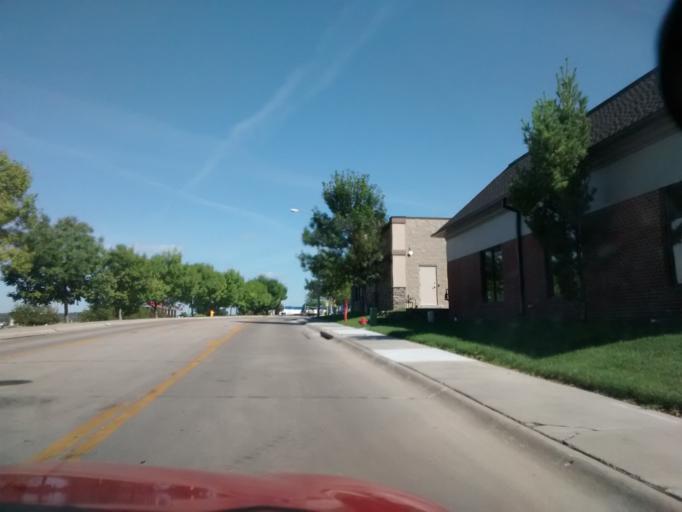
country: US
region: Nebraska
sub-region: Sarpy County
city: Offutt Air Force Base
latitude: 41.1409
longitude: -95.9714
